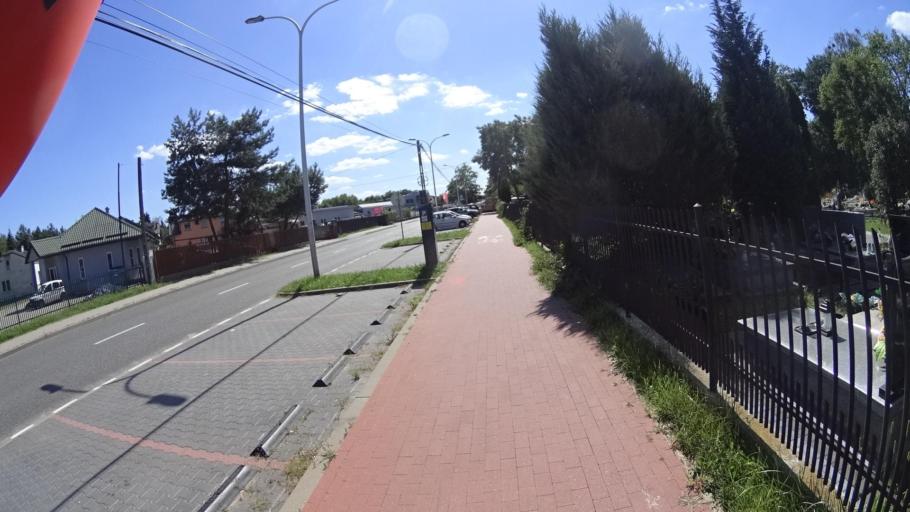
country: PL
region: Masovian Voivodeship
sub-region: Powiat piaseczynski
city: Piaseczno
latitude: 52.0816
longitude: 21.0411
